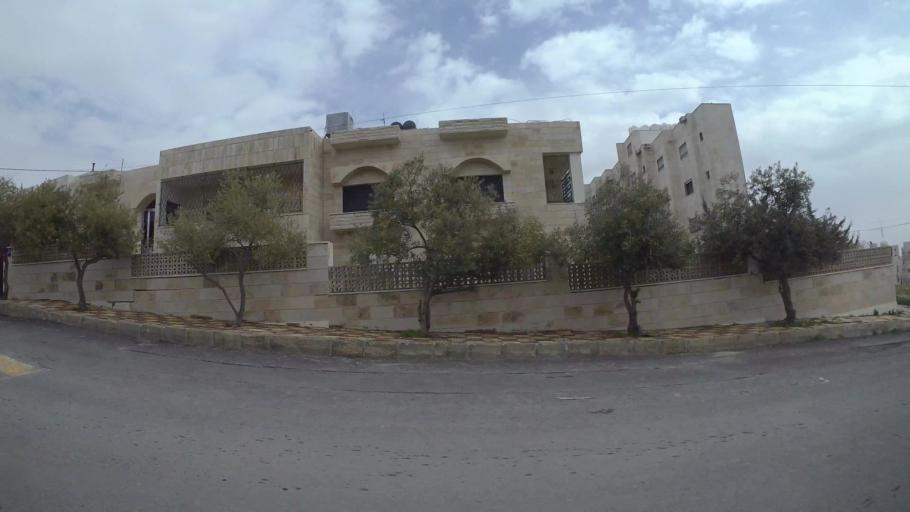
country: JO
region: Amman
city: Umm as Summaq
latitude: 31.9042
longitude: 35.8382
